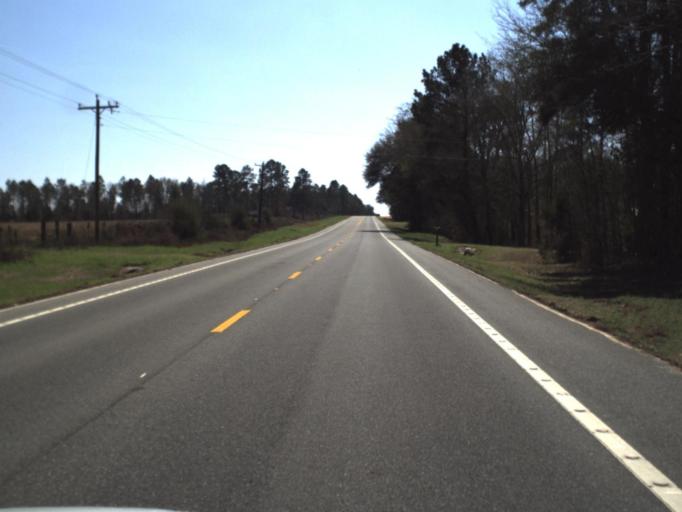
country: US
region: Florida
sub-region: Jackson County
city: Sneads
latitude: 30.6215
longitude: -85.0296
